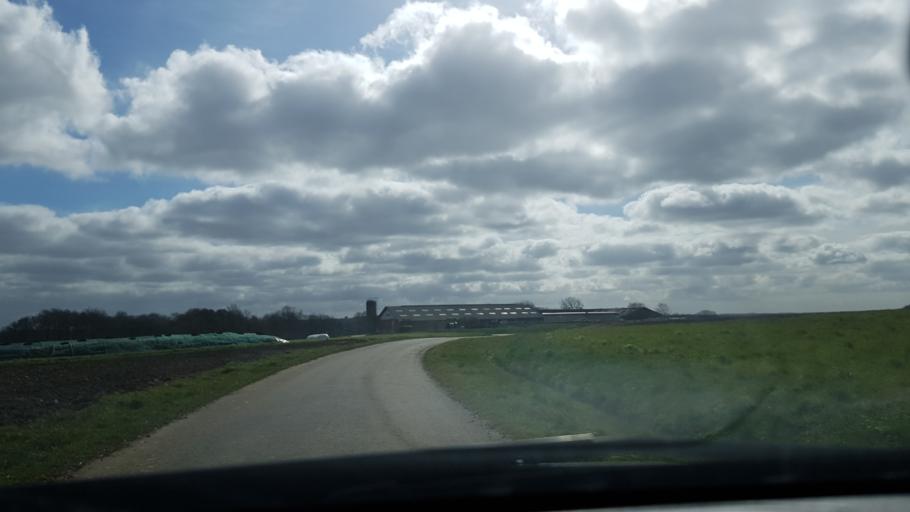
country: DK
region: South Denmark
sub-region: Haderslev Kommune
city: Gram
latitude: 55.3223
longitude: 8.9882
